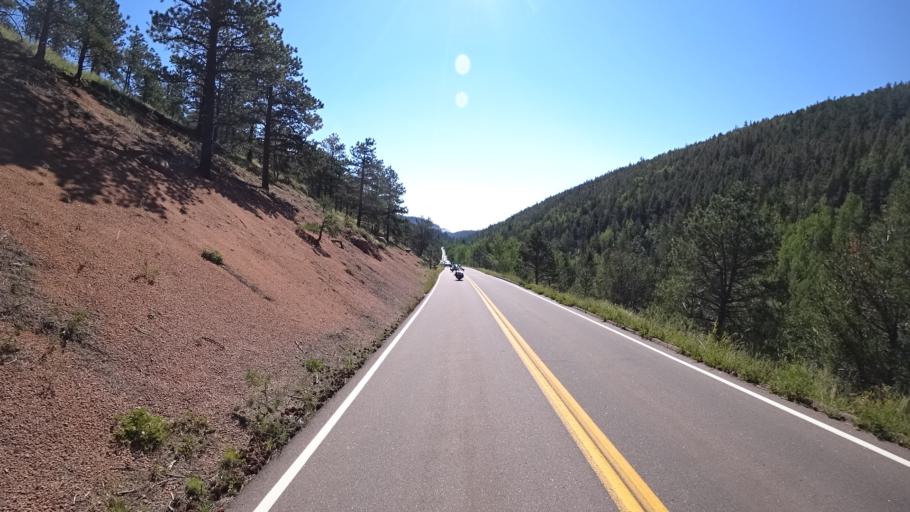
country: US
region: Colorado
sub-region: El Paso County
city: Cascade-Chipita Park
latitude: 38.9037
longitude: -105.0110
